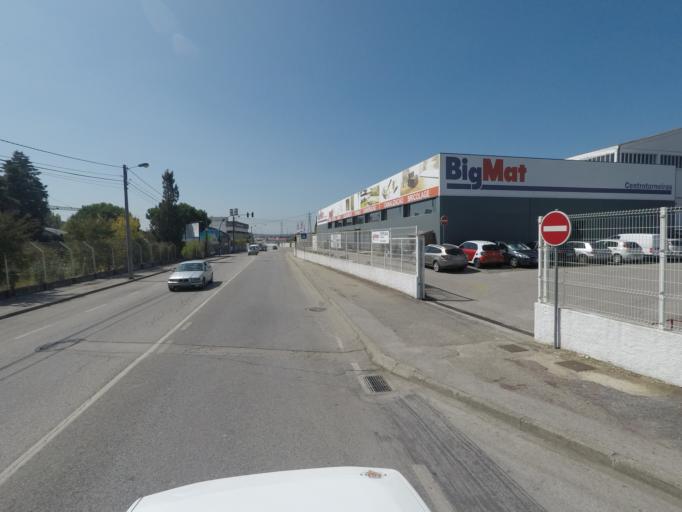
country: PT
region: Coimbra
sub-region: Coimbra
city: Coimbra
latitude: 40.2416
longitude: -8.4343
